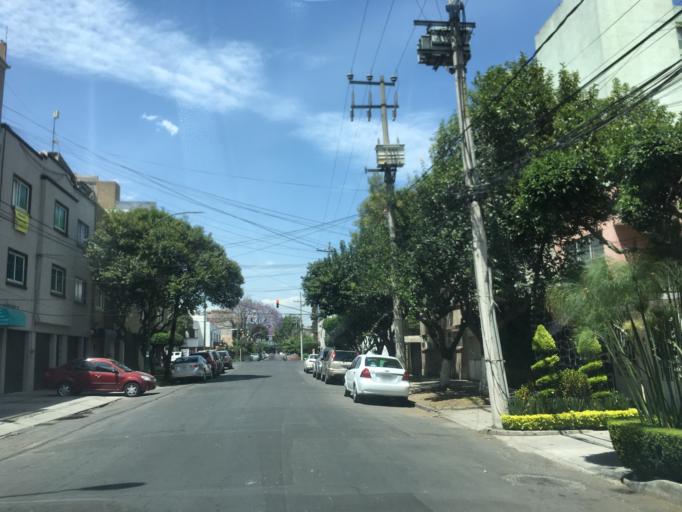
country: MX
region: Mexico City
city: Benito Juarez
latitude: 19.3979
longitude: -99.1601
